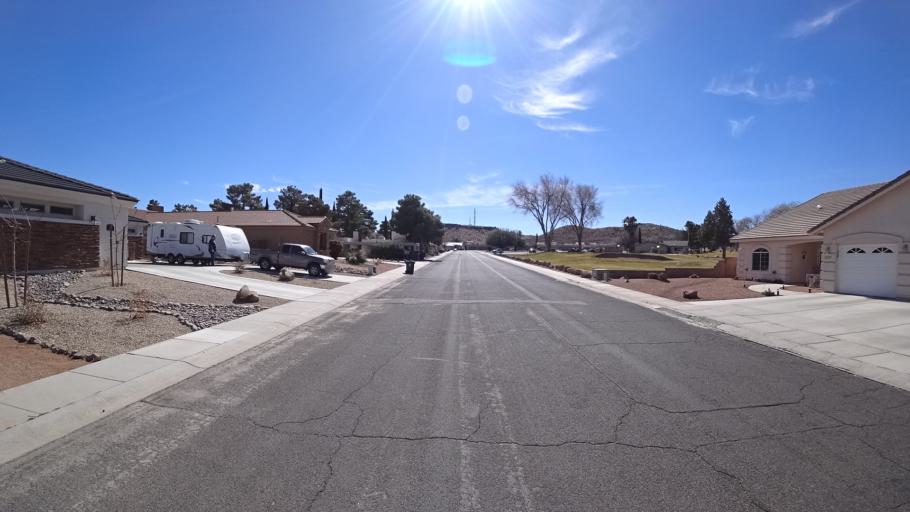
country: US
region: Arizona
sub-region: Mohave County
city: Kingman
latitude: 35.2080
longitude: -114.0413
